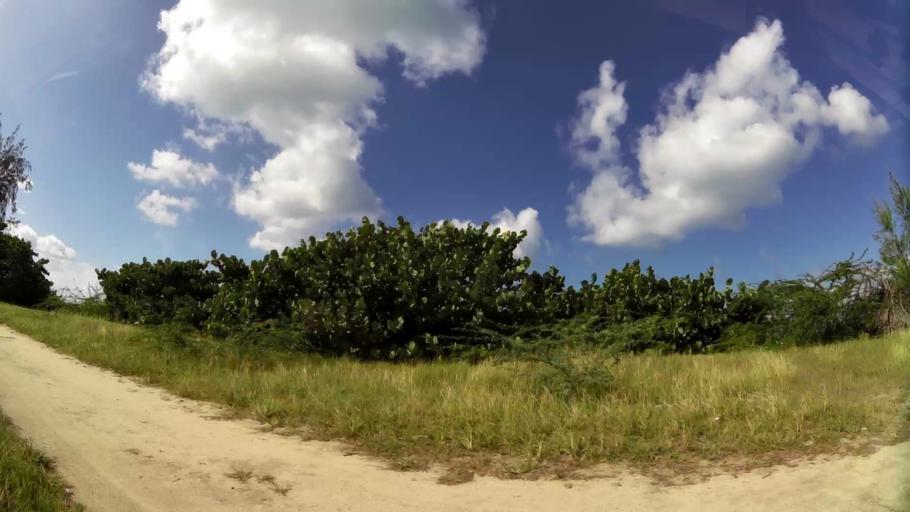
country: AG
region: Saint John
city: Saint John's
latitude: 17.1336
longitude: -61.8619
